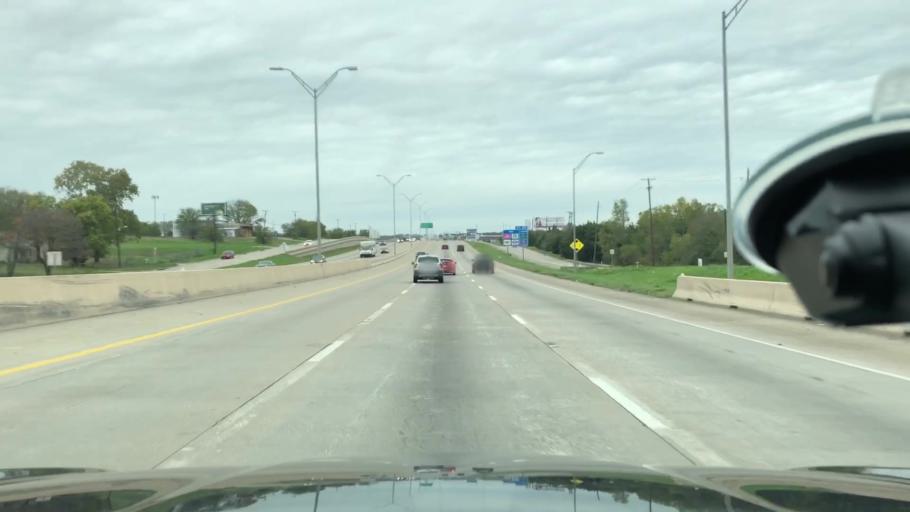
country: US
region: Texas
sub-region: Dallas County
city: DeSoto
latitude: 32.5802
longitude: -96.8223
